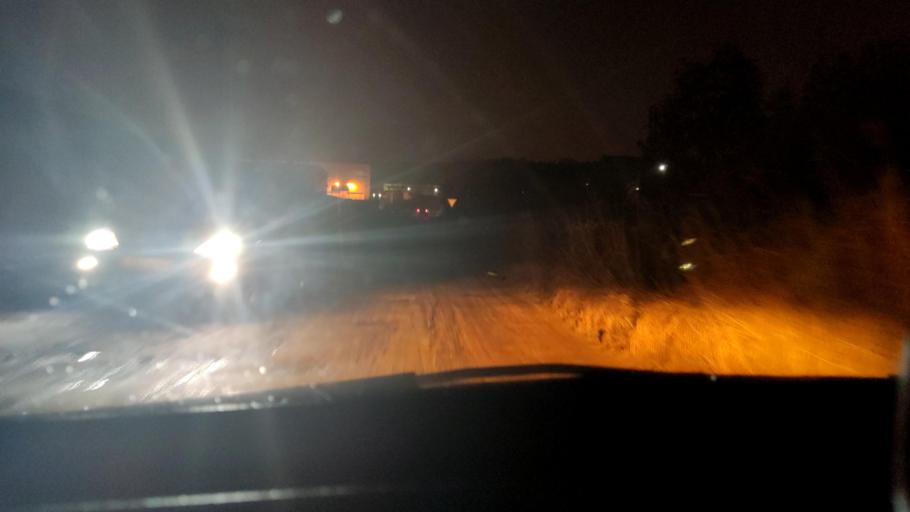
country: RU
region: Voronezj
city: Pridonskoy
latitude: 51.6384
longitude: 39.1102
